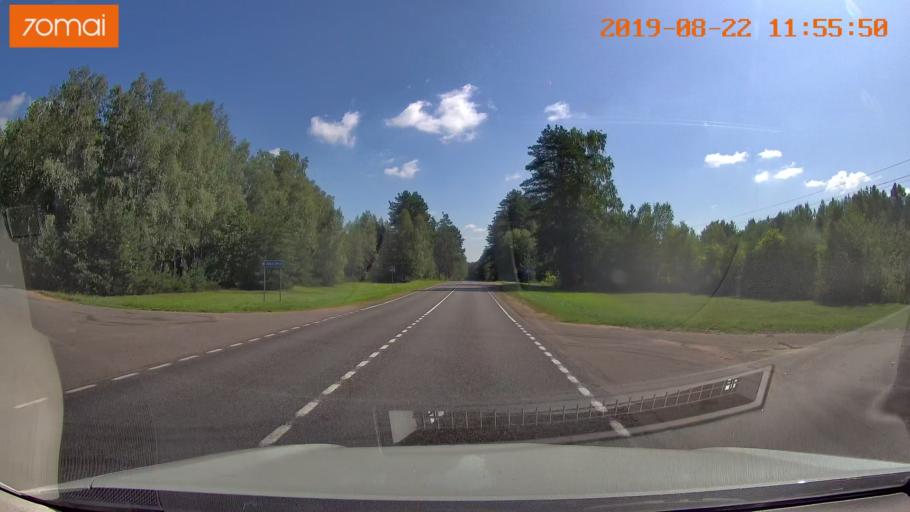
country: BY
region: Minsk
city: Prawdzinski
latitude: 53.4302
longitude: 27.5571
